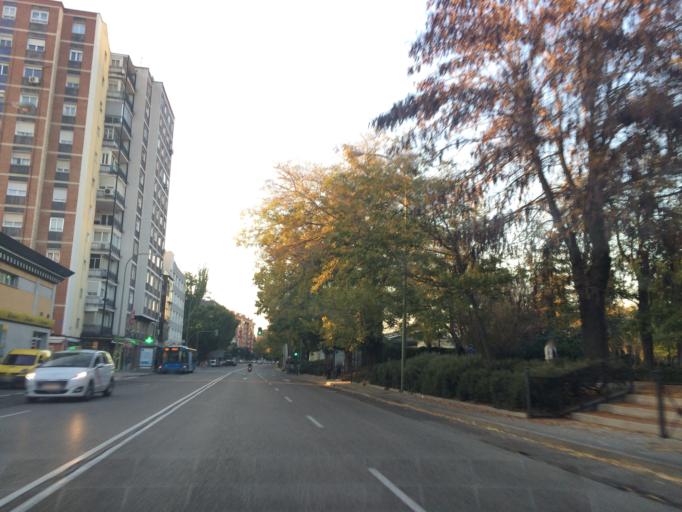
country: ES
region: Madrid
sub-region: Provincia de Madrid
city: Moncloa-Aravaca
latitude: 40.4280
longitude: -3.7290
